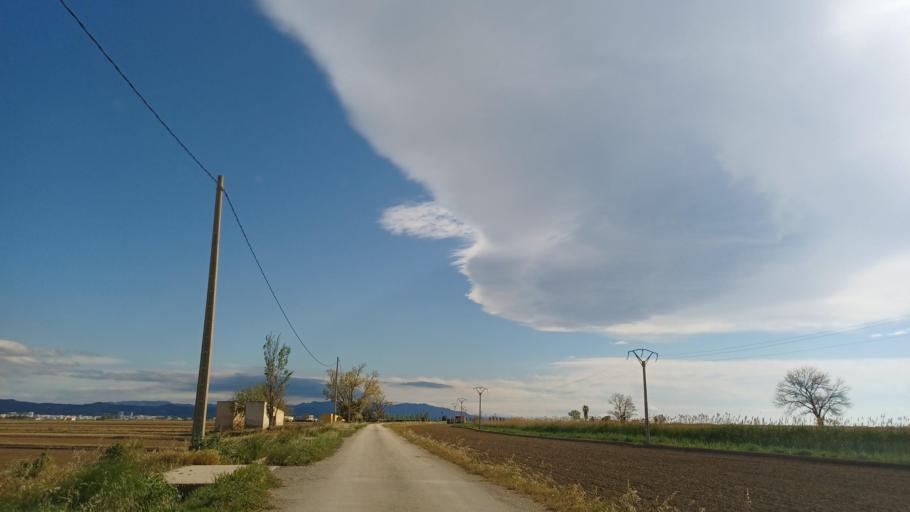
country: ES
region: Catalonia
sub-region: Provincia de Tarragona
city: L'Ampolla
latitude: 40.7712
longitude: 0.7088
